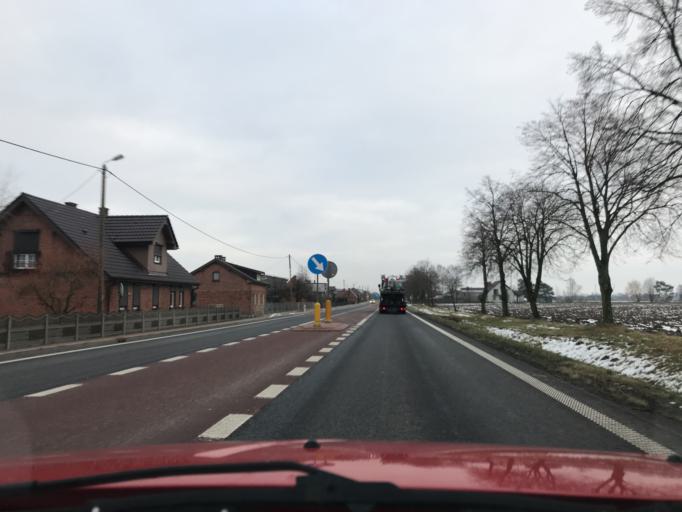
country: PL
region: Greater Poland Voivodeship
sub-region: Powiat pleszewski
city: Goluchow
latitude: 51.8690
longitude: 17.8967
